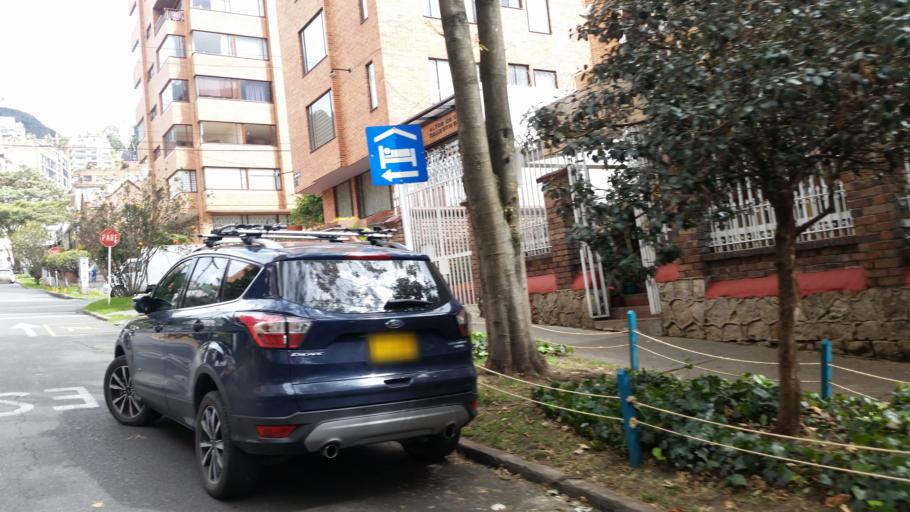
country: CO
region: Bogota D.C.
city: Bogota
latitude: 4.6423
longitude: -74.0614
